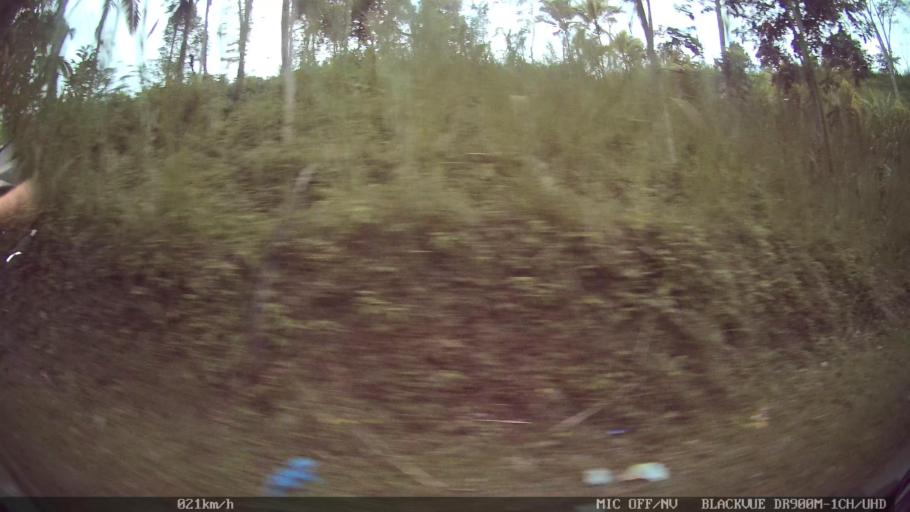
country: ID
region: Bali
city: Banjar Wangsian
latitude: -8.4602
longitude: 115.4157
